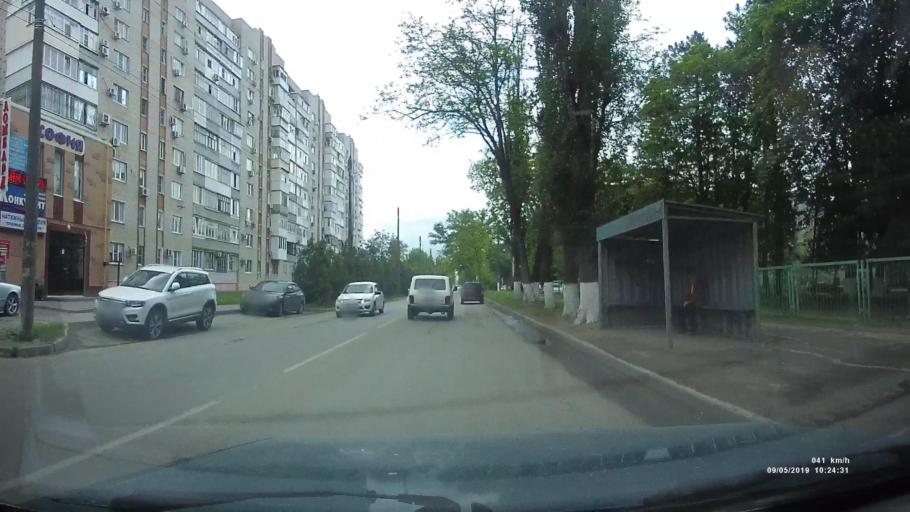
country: RU
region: Rostov
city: Azov
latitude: 47.0998
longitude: 39.4239
